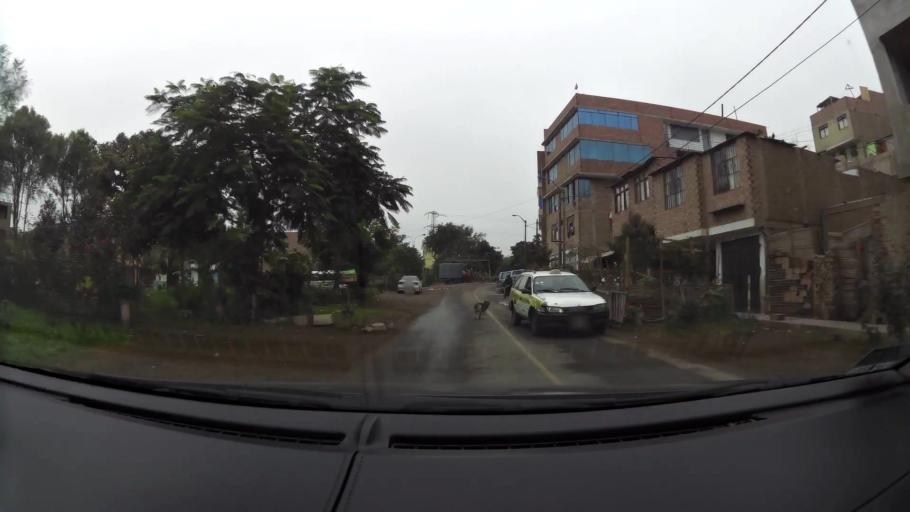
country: PE
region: Lima
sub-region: Lima
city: Independencia
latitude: -11.9705
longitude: -77.0833
